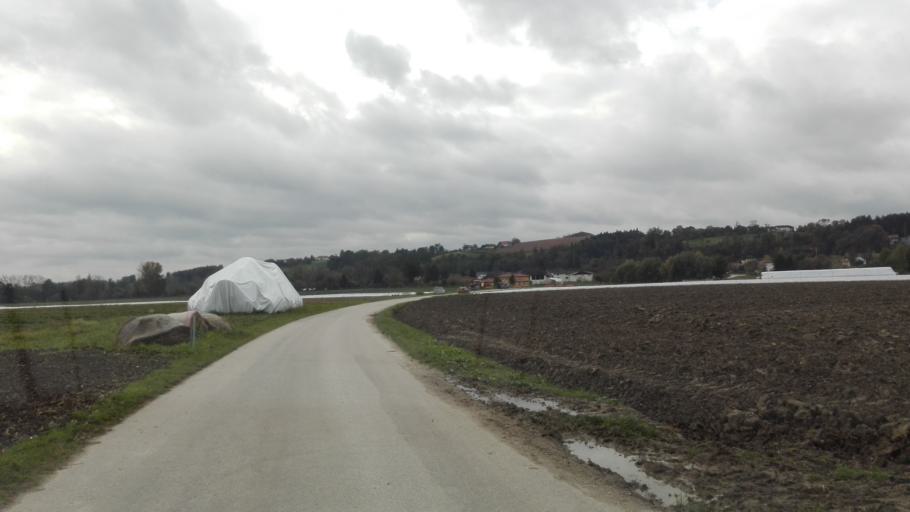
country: AT
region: Upper Austria
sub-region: Politischer Bezirk Urfahr-Umgebung
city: Feldkirchen an der Donau
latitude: 48.3272
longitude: 14.0069
